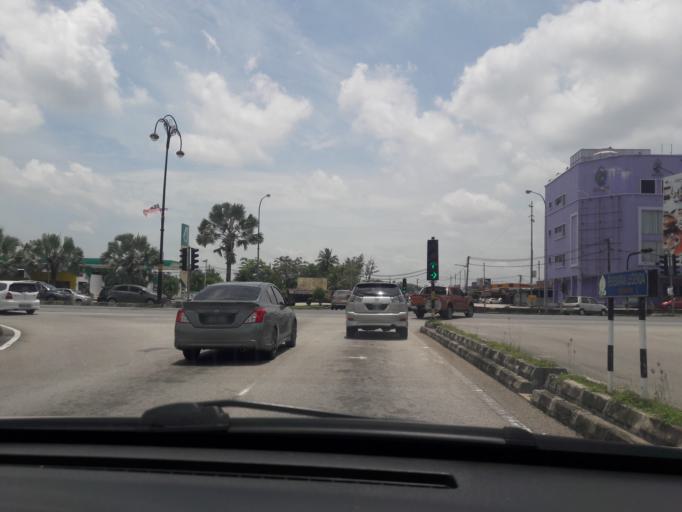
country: MY
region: Kedah
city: Sungai Petani
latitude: 5.6638
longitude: 100.5034
